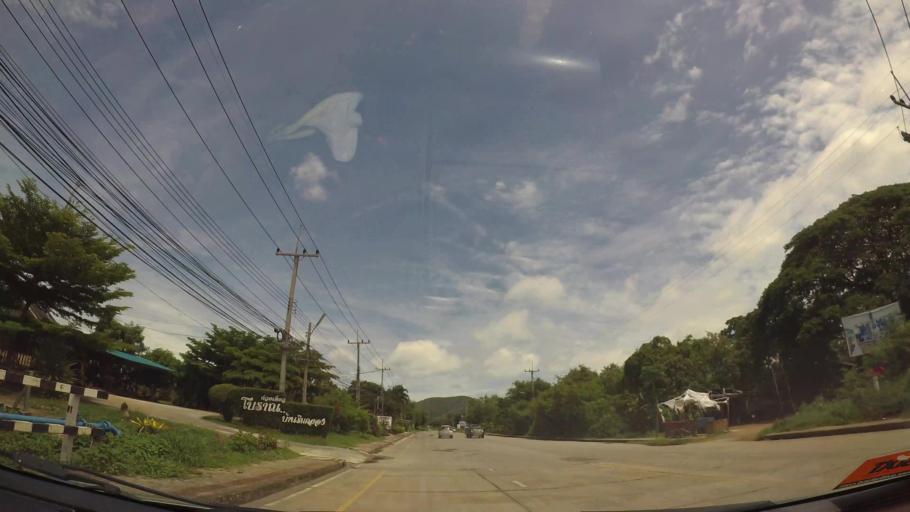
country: TH
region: Chon Buri
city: Sattahip
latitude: 12.7046
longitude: 100.8872
